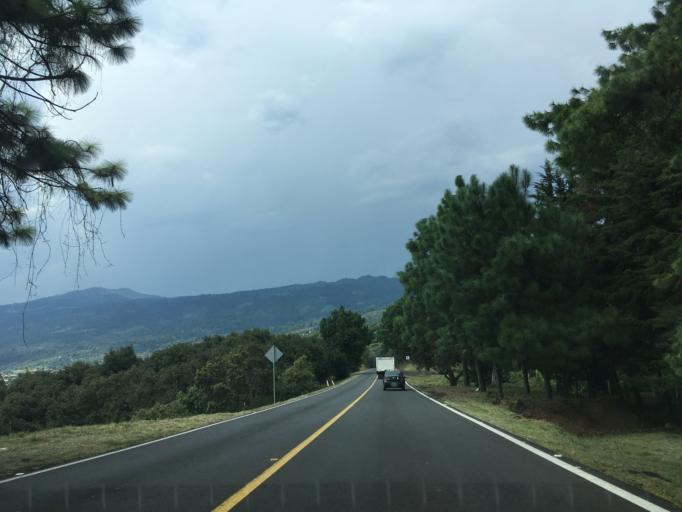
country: MX
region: Michoacan
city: Tingambato
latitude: 19.4967
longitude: -101.8384
